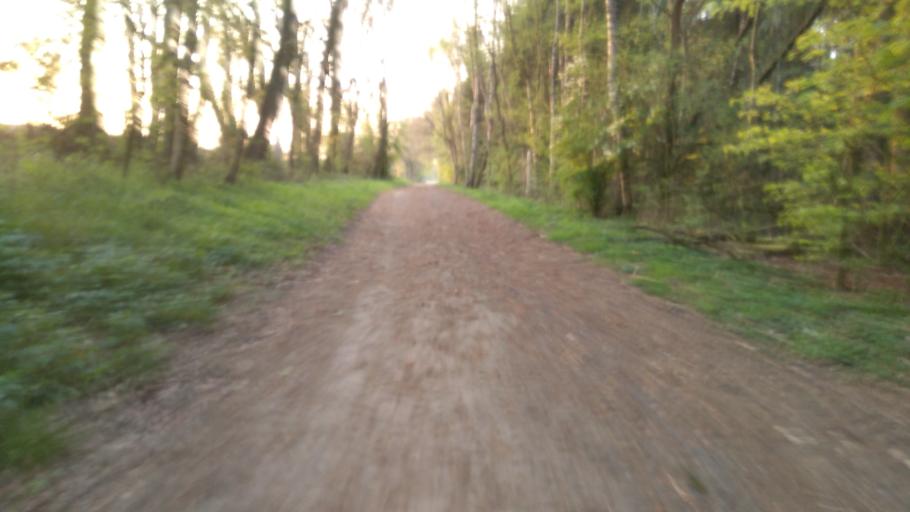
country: DE
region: Lower Saxony
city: Harsefeld
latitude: 53.4781
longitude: 9.5205
